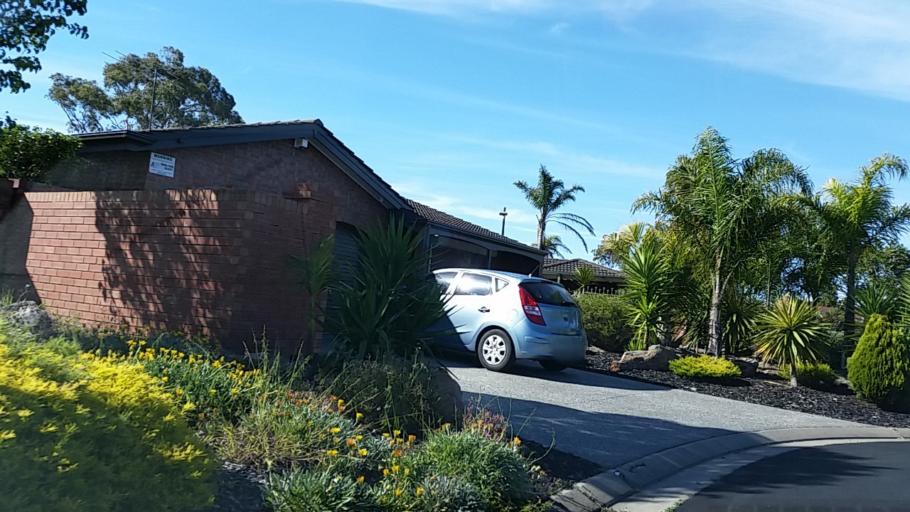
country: AU
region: South Australia
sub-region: Charles Sturt
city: West Lakes Shore
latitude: -34.8732
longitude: 138.4912
